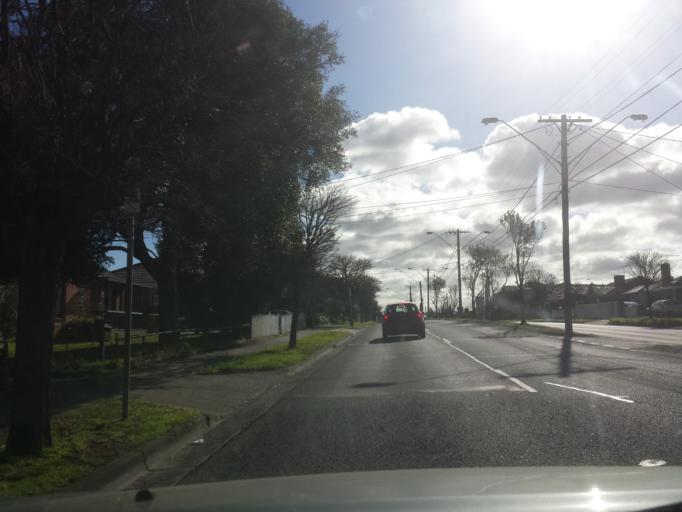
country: AU
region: Victoria
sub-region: Darebin
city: Preston
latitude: -37.7369
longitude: 145.0239
